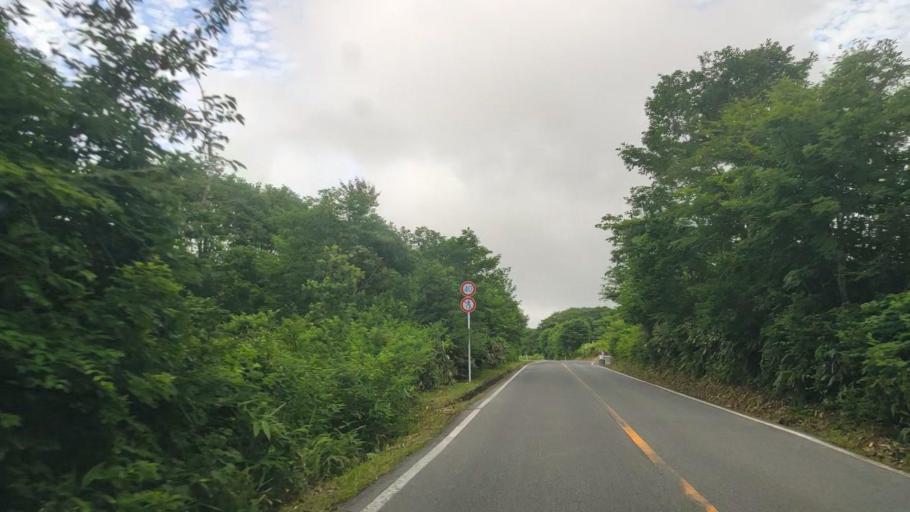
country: JP
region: Tottori
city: Kurayoshi
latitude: 35.3433
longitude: 133.5824
